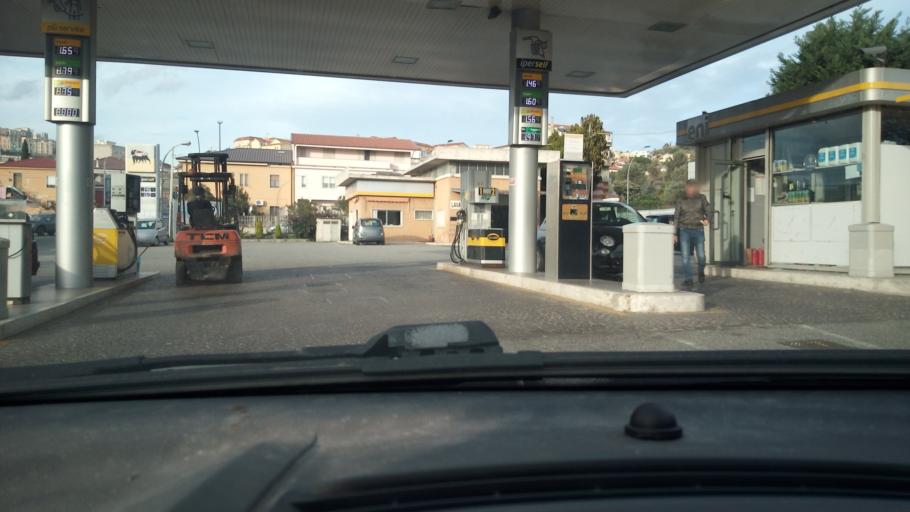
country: IT
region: Calabria
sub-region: Provincia di Catanzaro
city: Catanzaro
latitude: 38.8890
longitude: 16.6028
